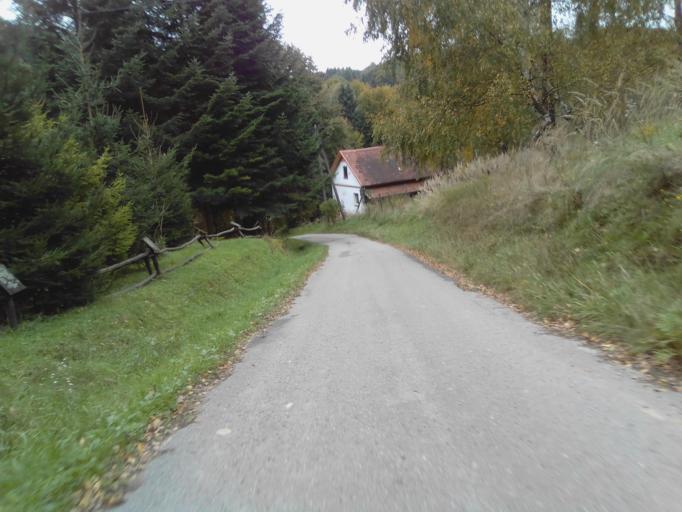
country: PL
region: Subcarpathian Voivodeship
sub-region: Powiat strzyzowski
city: Strzyzow
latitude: 49.8521
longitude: 21.8356
